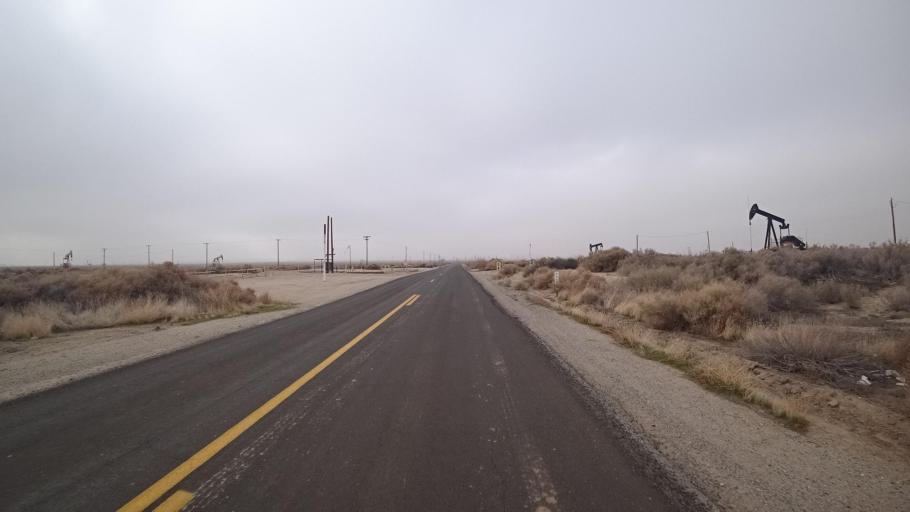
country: US
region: California
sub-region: Kern County
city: Maricopa
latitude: 35.0756
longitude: -119.3601
